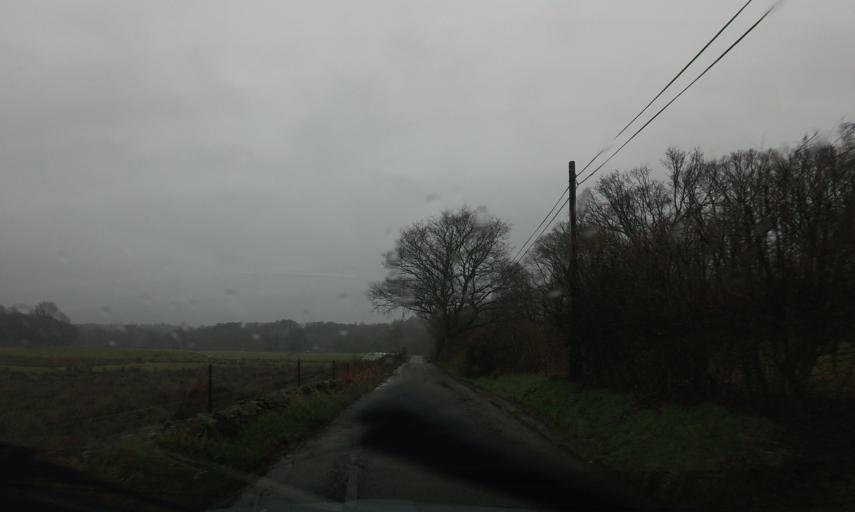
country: GB
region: Scotland
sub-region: West Dunbartonshire
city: Balloch
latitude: 56.1391
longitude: -4.6186
